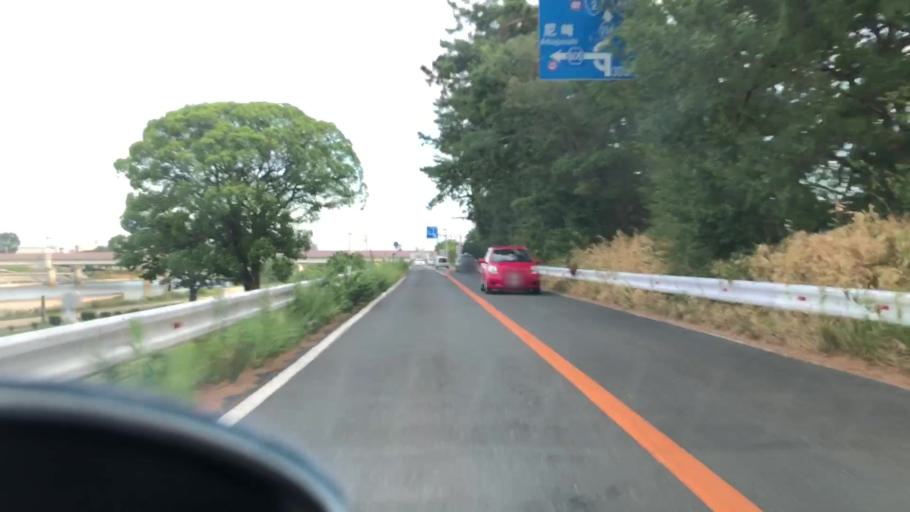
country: JP
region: Hyogo
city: Itami
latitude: 34.7513
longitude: 135.3733
